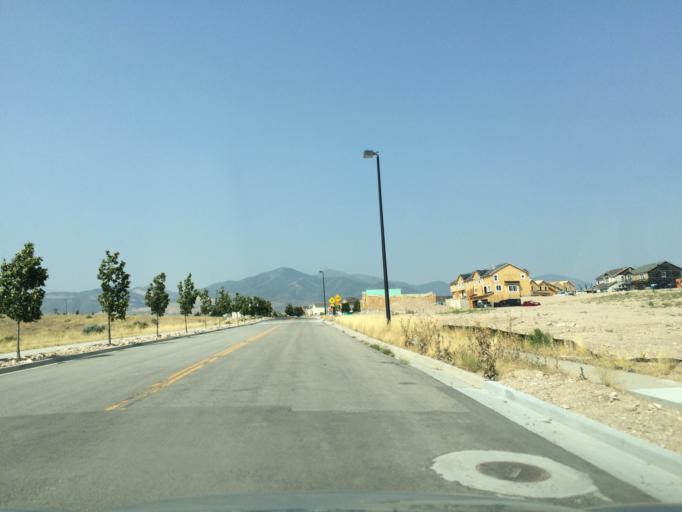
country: US
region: Utah
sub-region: Salt Lake County
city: Oquirrh
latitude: 40.6106
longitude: -112.0478
